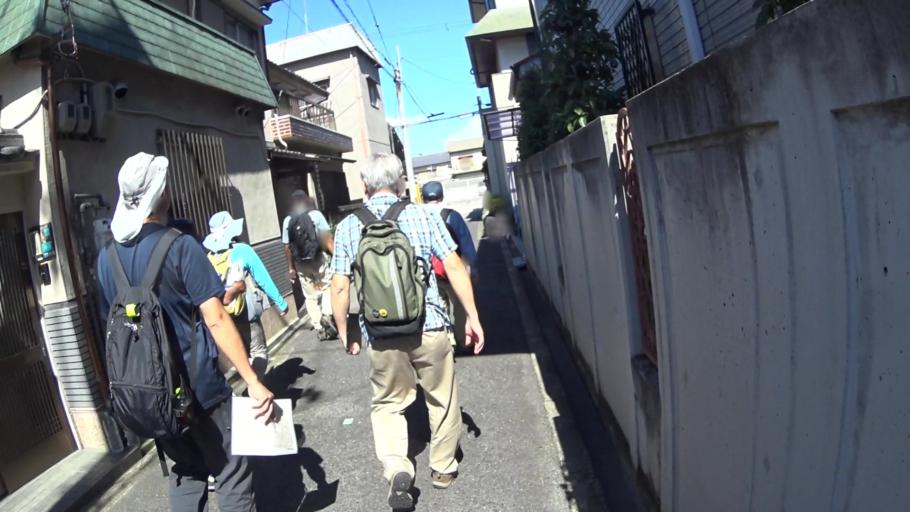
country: JP
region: Osaka
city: Yao
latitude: 34.6319
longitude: 135.5576
